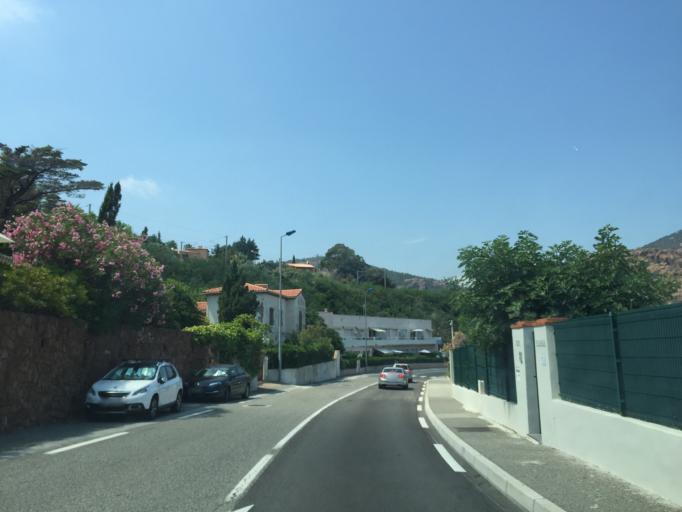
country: FR
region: Provence-Alpes-Cote d'Azur
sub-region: Departement des Alpes-Maritimes
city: Theoule-sur-Mer
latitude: 43.4350
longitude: 6.8931
